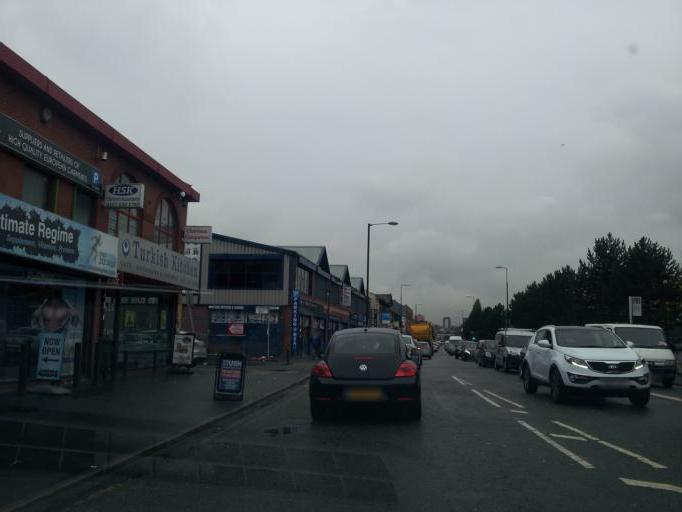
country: GB
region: England
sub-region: Manchester
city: Cheetham Hill
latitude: 53.4913
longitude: -2.2480
